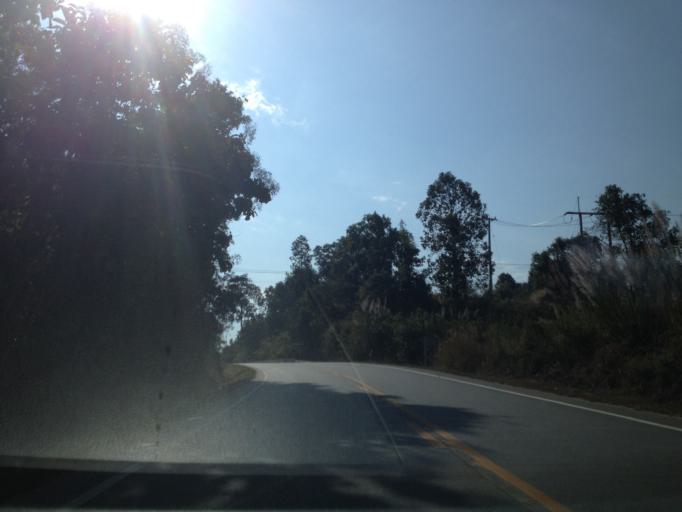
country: TH
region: Mae Hong Son
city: Pa Pae
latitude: 18.1663
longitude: 98.2314
